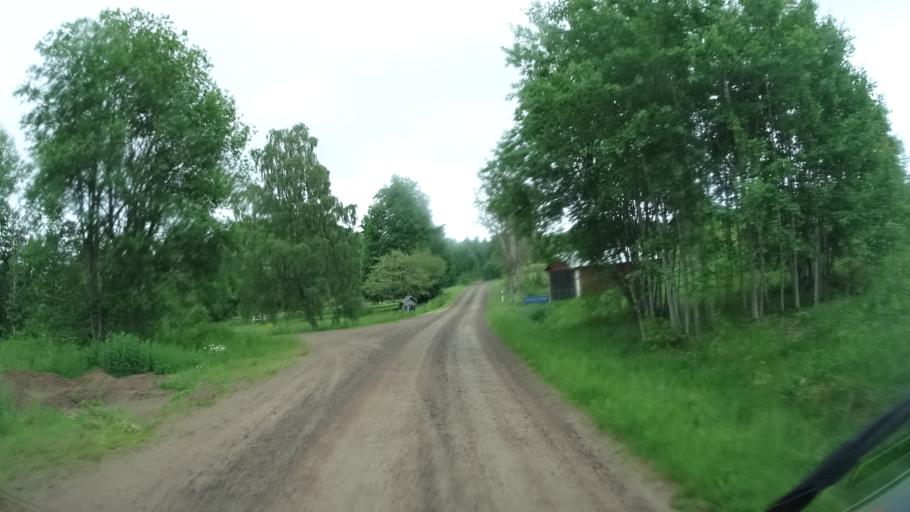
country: SE
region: Joenkoeping
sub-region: Eksjo Kommun
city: Mariannelund
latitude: 57.6192
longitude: 15.6546
